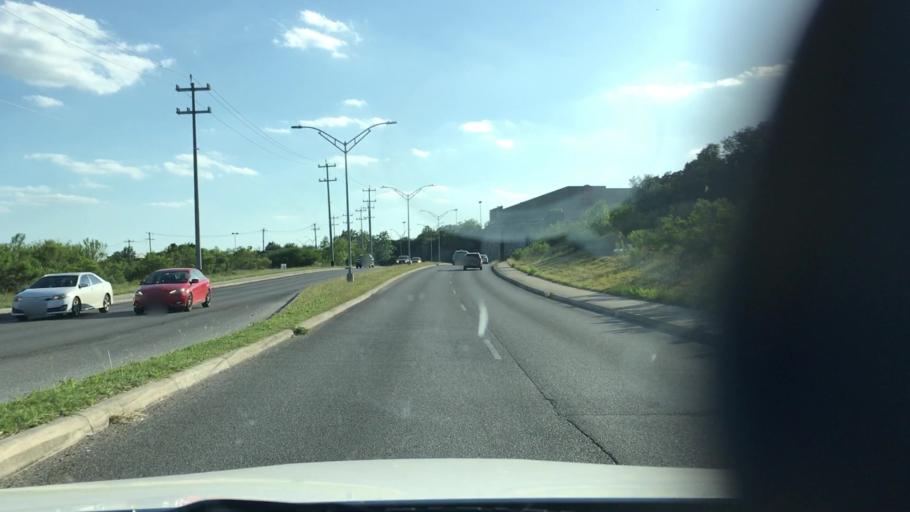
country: US
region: Texas
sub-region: Bexar County
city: Timberwood Park
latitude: 29.6541
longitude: -98.4417
